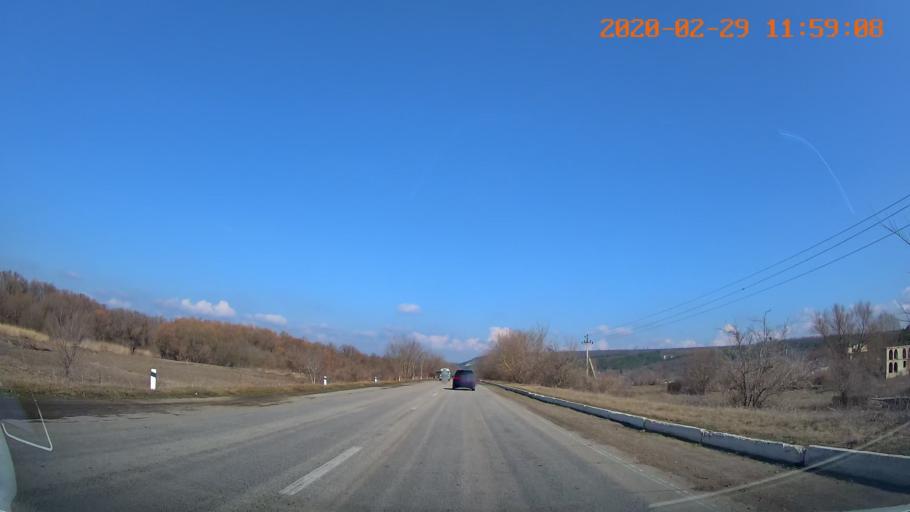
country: MD
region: Telenesti
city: Ribnita
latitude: 47.8215
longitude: 29.0151
